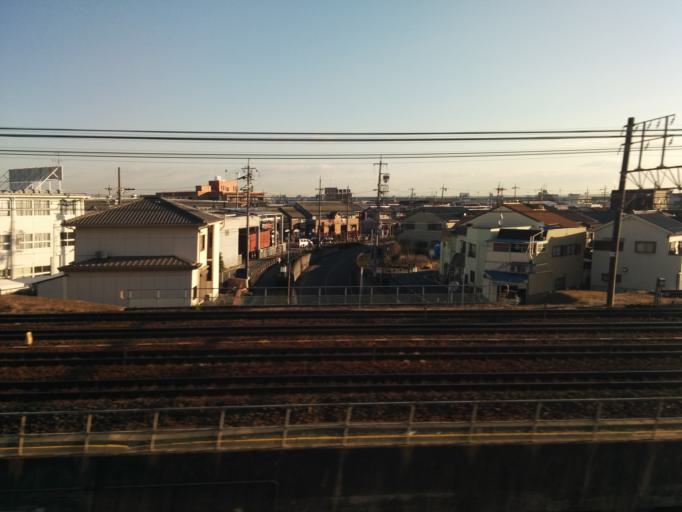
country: JP
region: Aichi
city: Inazawa
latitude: 35.2152
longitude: 136.8434
